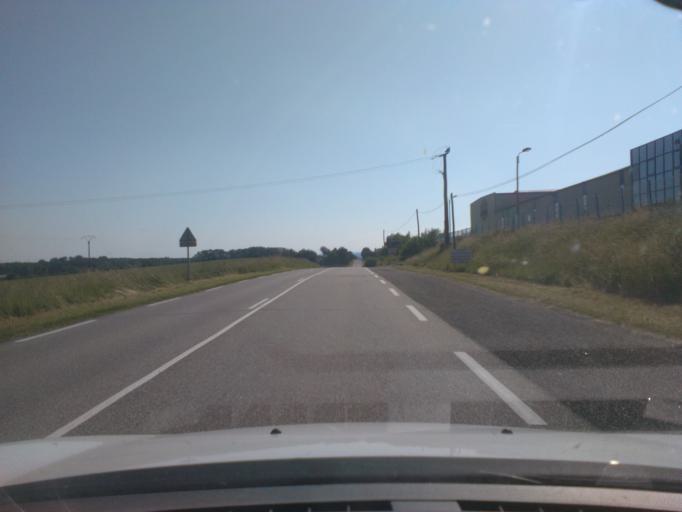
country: FR
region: Lorraine
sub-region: Departement des Vosges
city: Aydoilles
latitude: 48.2093
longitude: 6.5565
